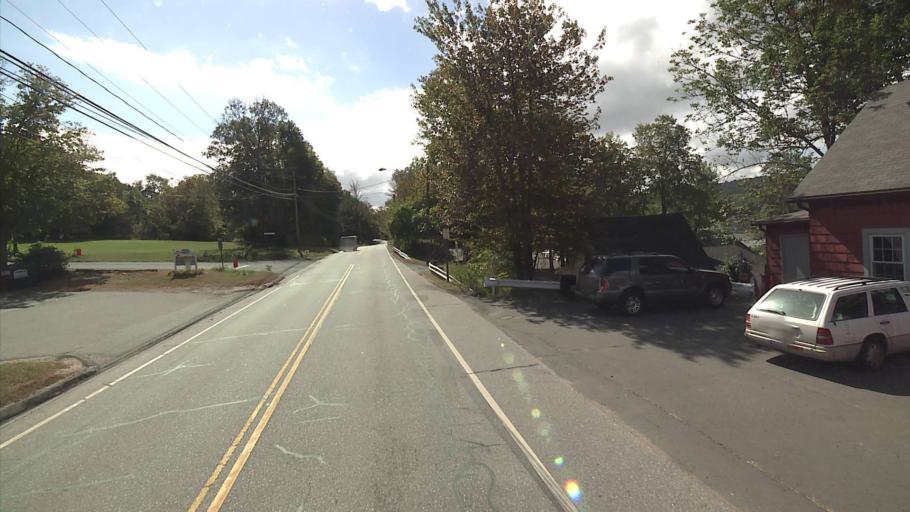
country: US
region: Connecticut
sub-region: Middlesex County
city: Durham
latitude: 41.5174
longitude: -72.7284
